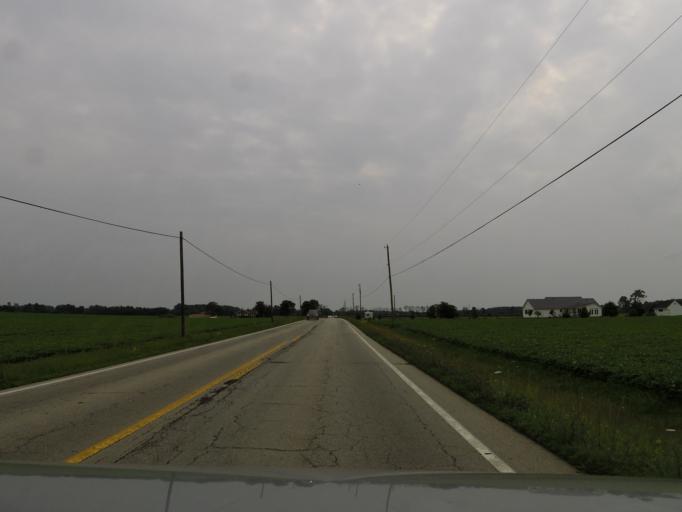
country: US
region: Ohio
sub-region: Clinton County
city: Blanchester
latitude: 39.3271
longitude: -83.8992
